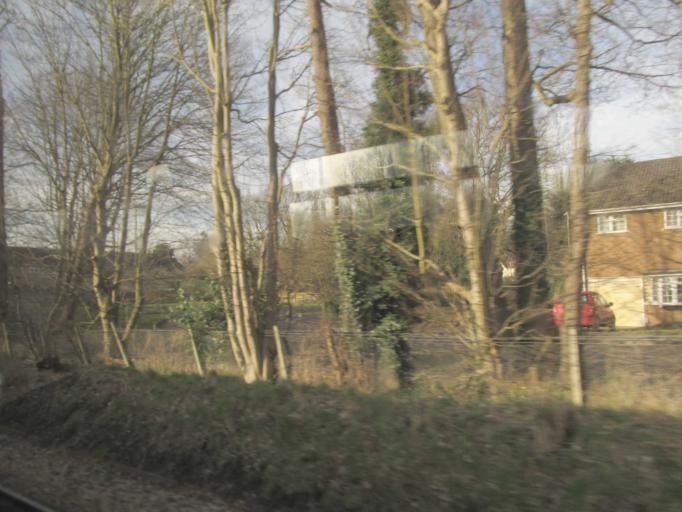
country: GB
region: England
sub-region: Hampshire
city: Farnborough
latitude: 51.2944
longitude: -0.7402
